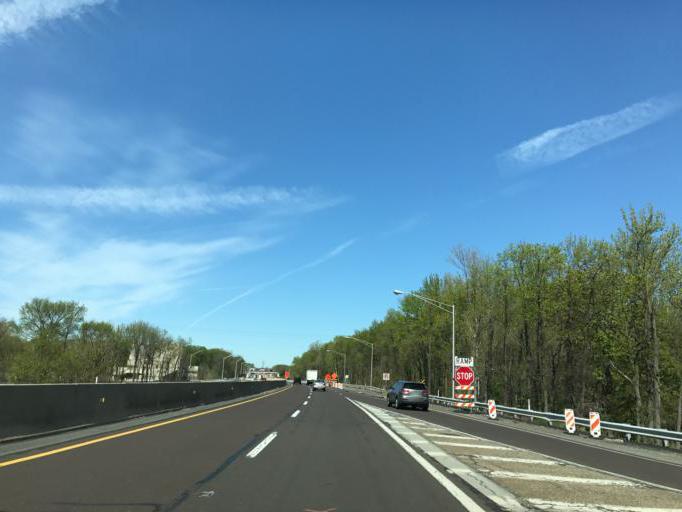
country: US
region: Pennsylvania
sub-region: Bucks County
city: Bristol
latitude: 40.1235
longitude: -74.8530
